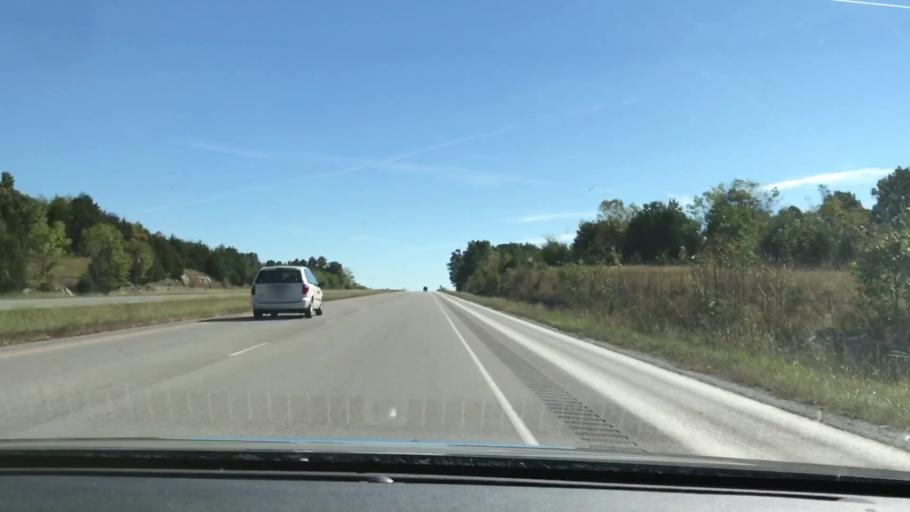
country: US
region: Kentucky
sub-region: Todd County
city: Elkton
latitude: 36.8474
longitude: -87.3171
